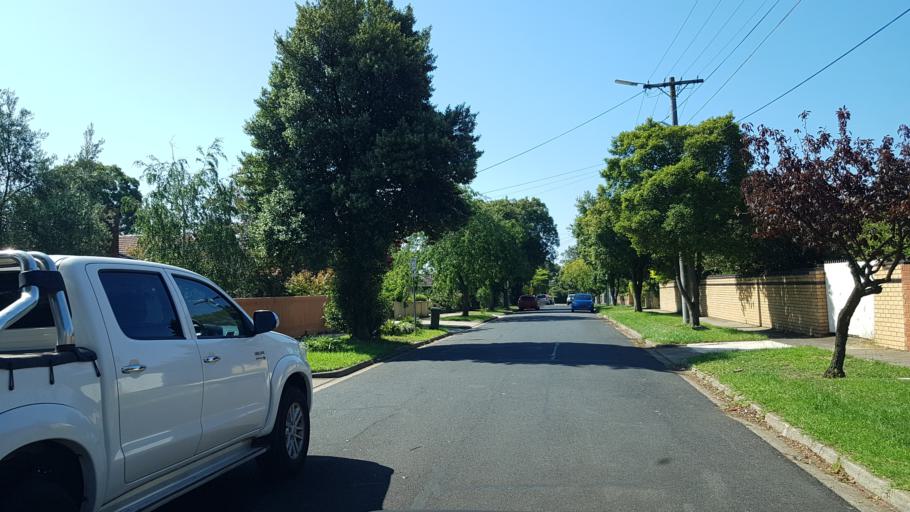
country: AU
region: Victoria
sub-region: Banyule
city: Heidelberg Heights
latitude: -37.7495
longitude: 145.0562
